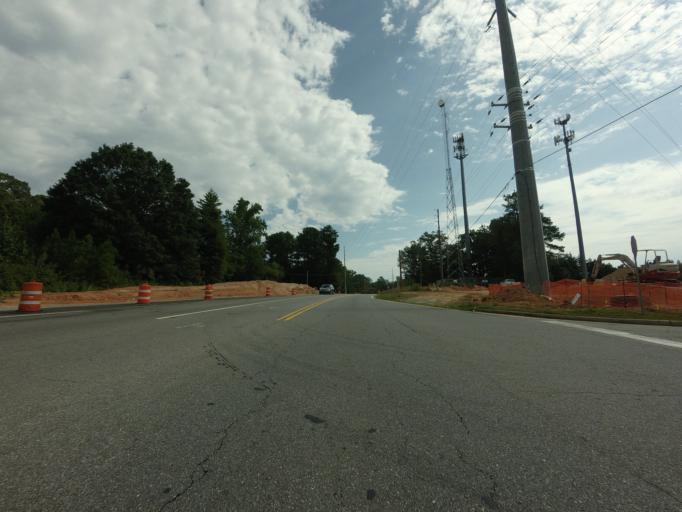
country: US
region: Georgia
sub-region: Gwinnett County
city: Duluth
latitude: 34.0579
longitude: -84.1310
